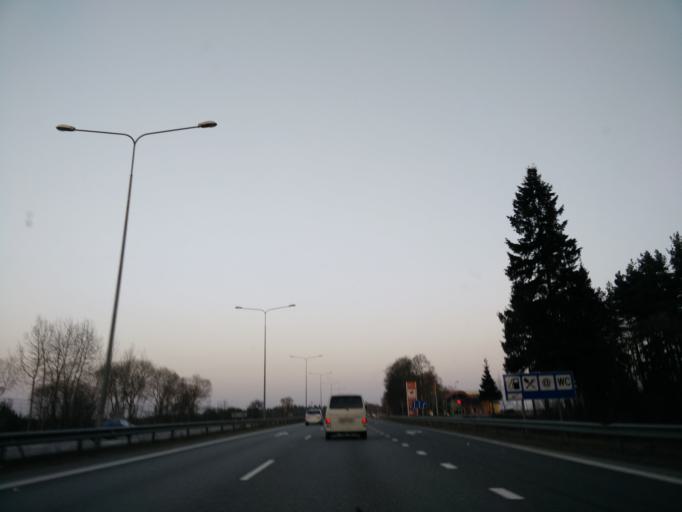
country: LT
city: Lentvaris
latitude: 54.7091
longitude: 24.9934
